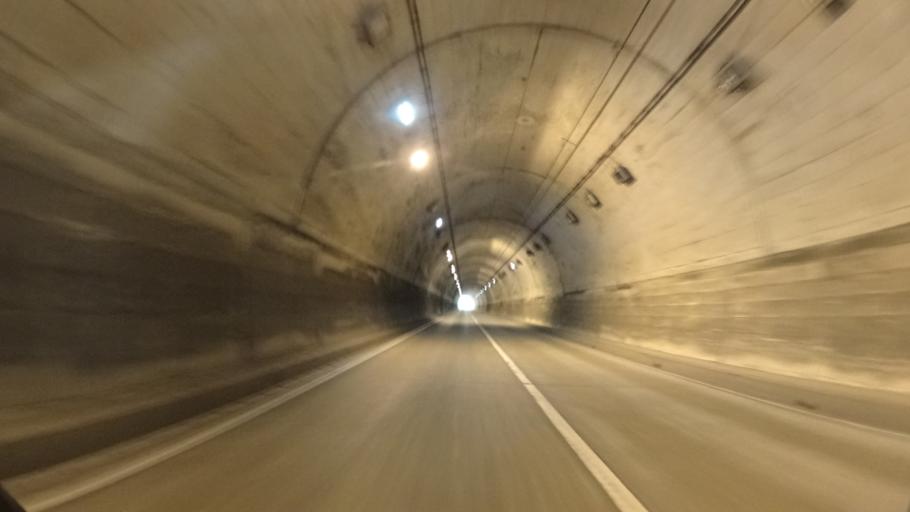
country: JP
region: Ehime
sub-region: Nishiuwa-gun
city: Ikata-cho
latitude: 33.4867
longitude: 132.3369
